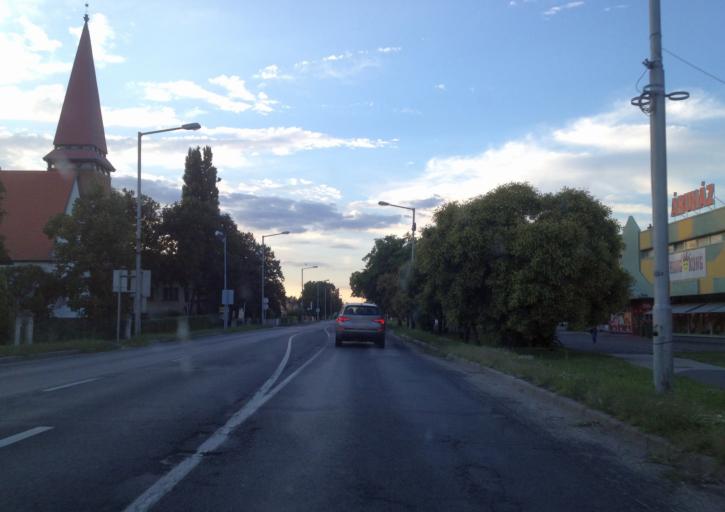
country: HU
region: Gyor-Moson-Sopron
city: Mosonmagyarovar
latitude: 47.8670
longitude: 17.2721
